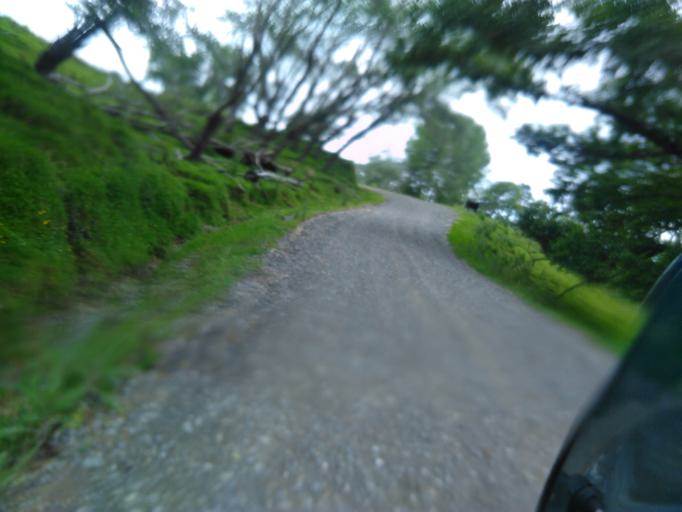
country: NZ
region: Gisborne
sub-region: Gisborne District
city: Gisborne
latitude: -38.0742
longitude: 178.0524
